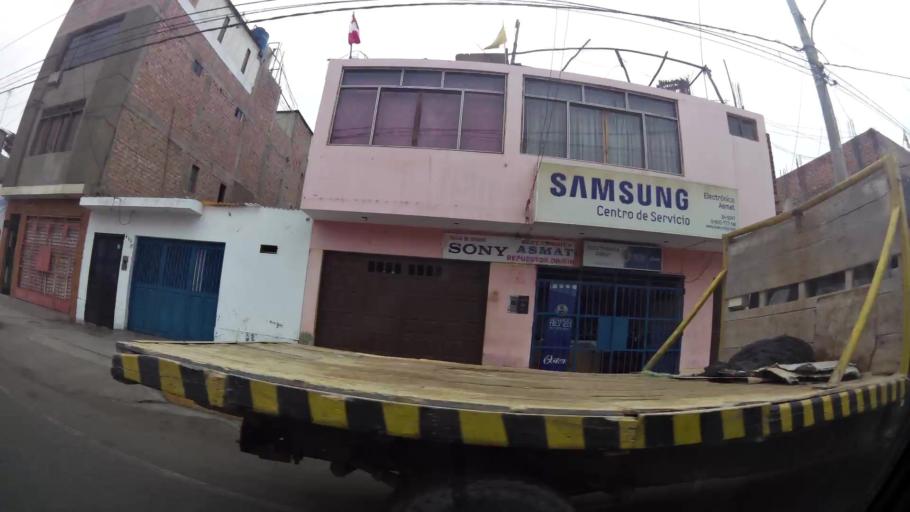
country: PE
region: Ancash
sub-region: Provincia de Santa
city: Chimbote
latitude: -9.0709
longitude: -78.5927
